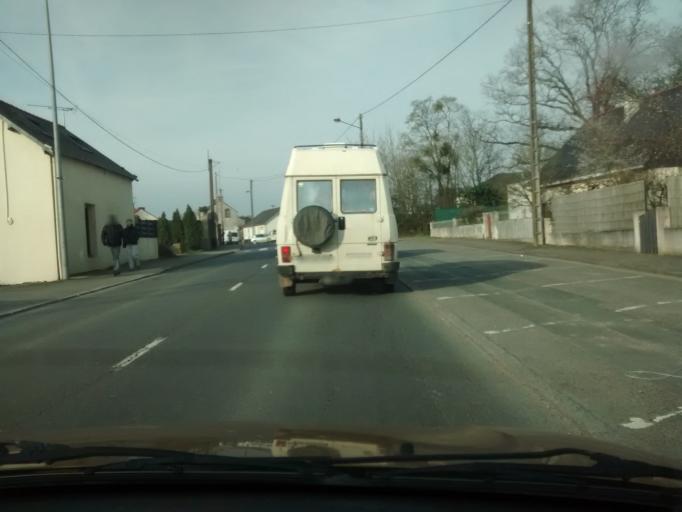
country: FR
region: Pays de la Loire
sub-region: Departement de la Loire-Atlantique
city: Heric
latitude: 47.4149
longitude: -1.6490
